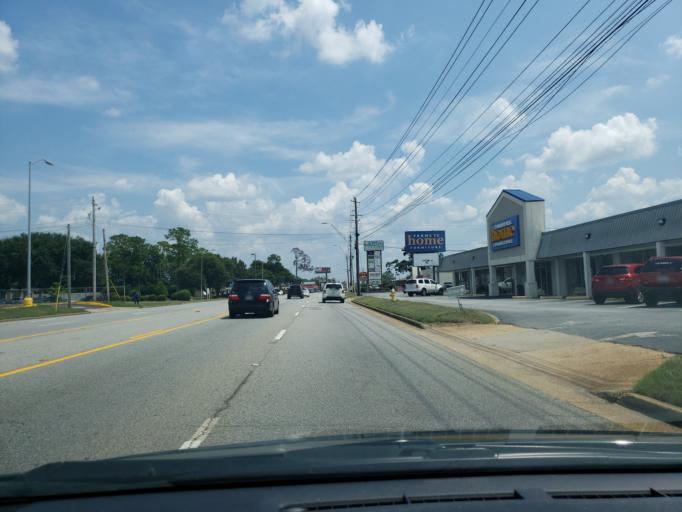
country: US
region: Georgia
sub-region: Dougherty County
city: Albany
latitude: 31.6113
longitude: -84.2130
